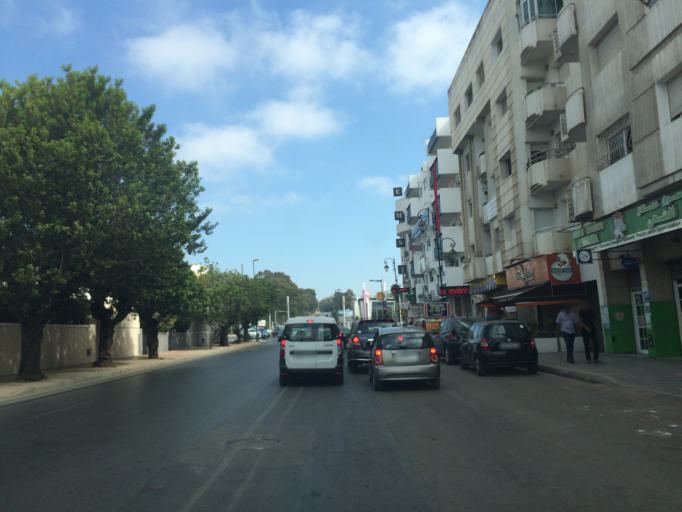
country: MA
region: Rabat-Sale-Zemmour-Zaer
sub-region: Rabat
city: Rabat
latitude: 34.0002
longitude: -6.8447
